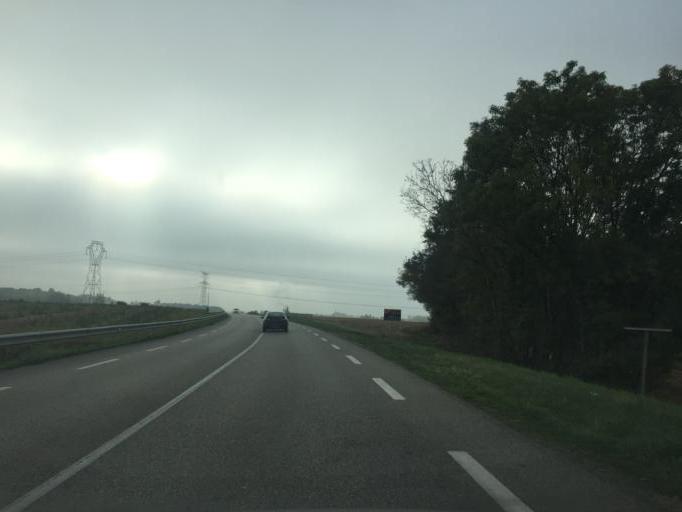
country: FR
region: Rhone-Alpes
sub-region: Departement de l'Ain
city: Saint-Andre-de-Corcy
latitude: 45.9428
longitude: 4.9744
